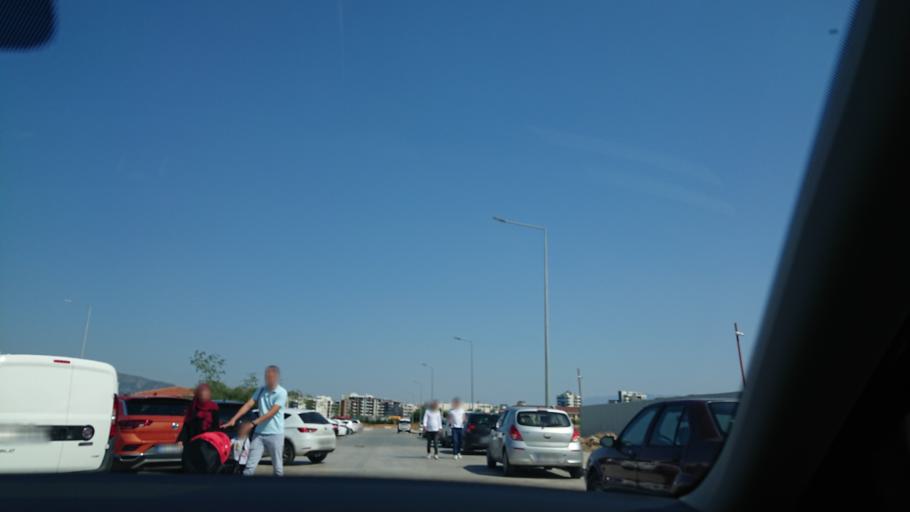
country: TR
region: Izmir
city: Karsiyaka
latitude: 38.4737
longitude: 27.0766
